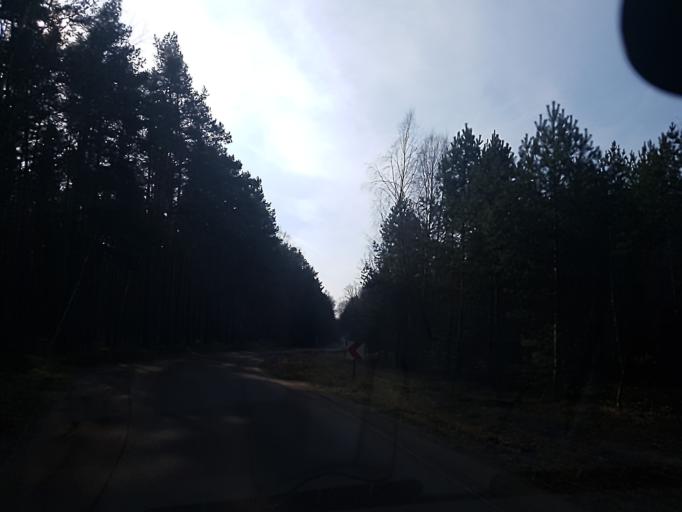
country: DE
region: Brandenburg
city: Wenzlow
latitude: 52.3526
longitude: 12.4652
